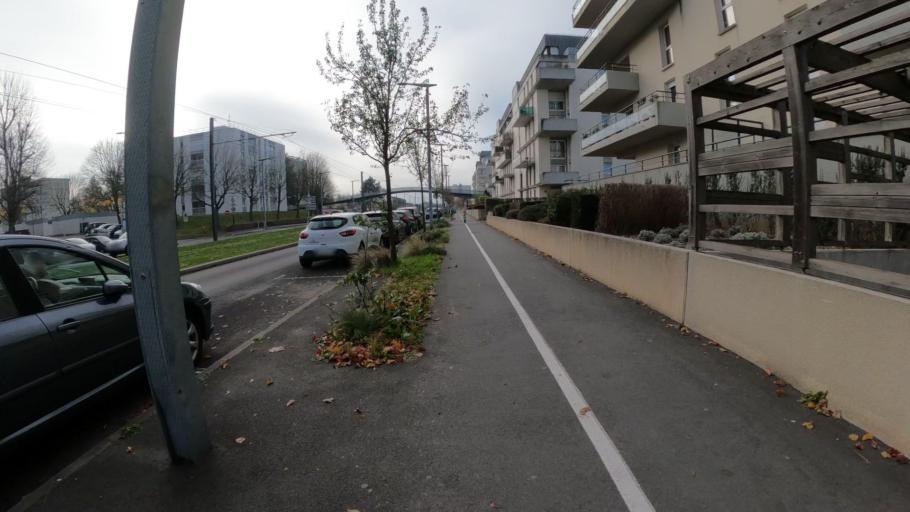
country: FR
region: Lower Normandy
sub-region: Departement du Calvados
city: Caen
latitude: 49.2021
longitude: -0.3418
